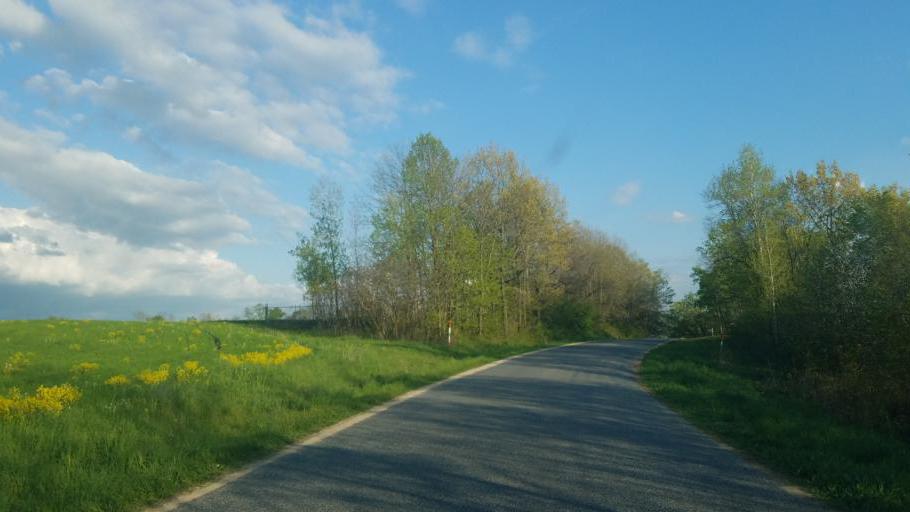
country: US
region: Wisconsin
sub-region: Vernon County
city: Hillsboro
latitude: 43.6716
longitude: -90.3541
